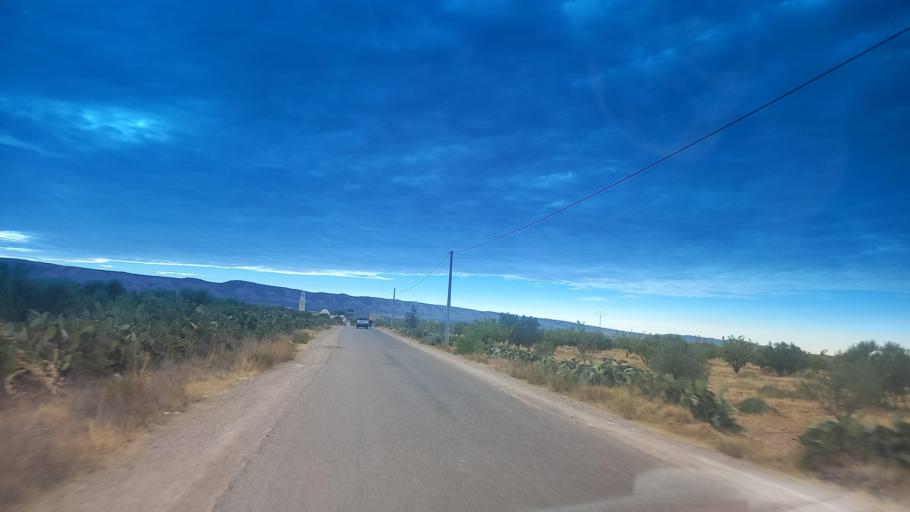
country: TN
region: Al Qasrayn
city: Sbiba
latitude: 35.3645
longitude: 9.0864
